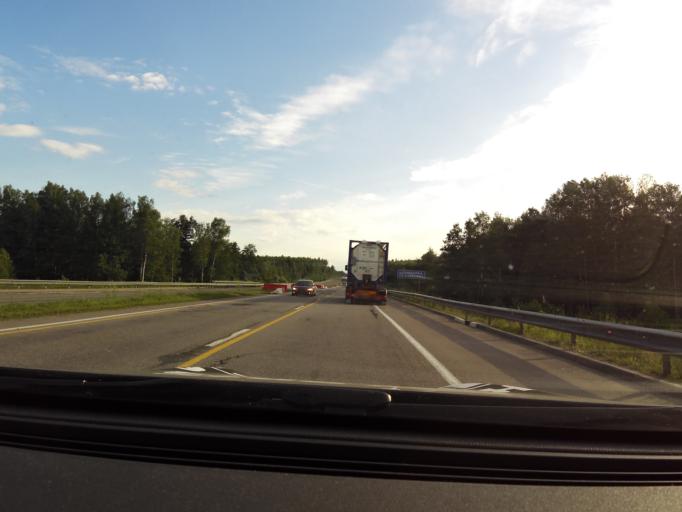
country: RU
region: Vladimir
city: Sudogda
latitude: 56.1244
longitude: 40.8642
